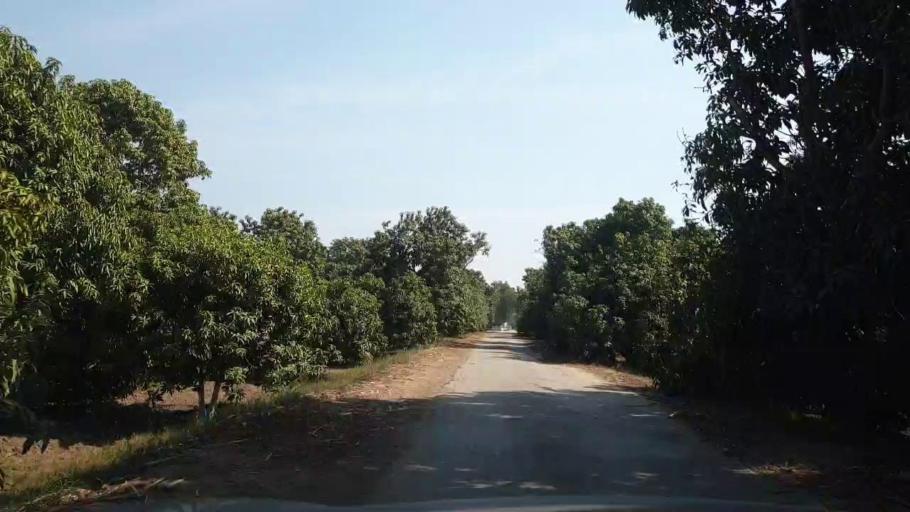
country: PK
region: Sindh
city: Tando Adam
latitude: 25.6269
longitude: 68.7367
